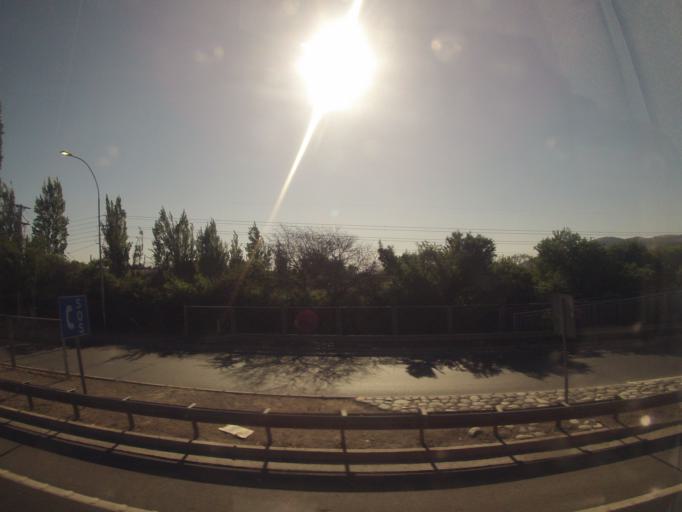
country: CL
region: Santiago Metropolitan
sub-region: Provincia de Maipo
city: San Bernardo
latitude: -33.6238
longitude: -70.7146
